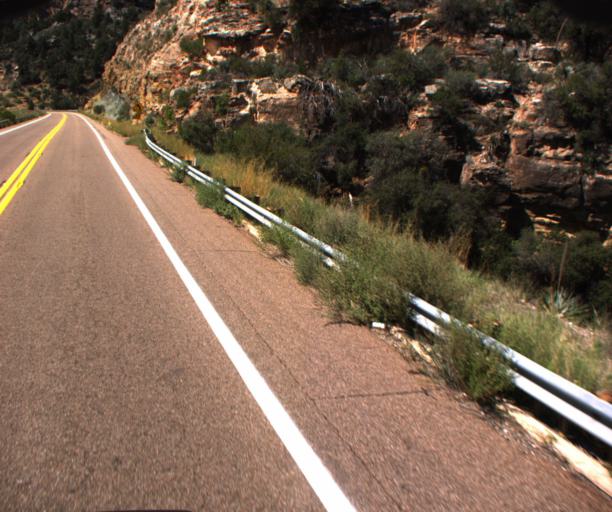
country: US
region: Arizona
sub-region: Navajo County
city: Cibecue
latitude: 33.8191
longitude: -110.4629
